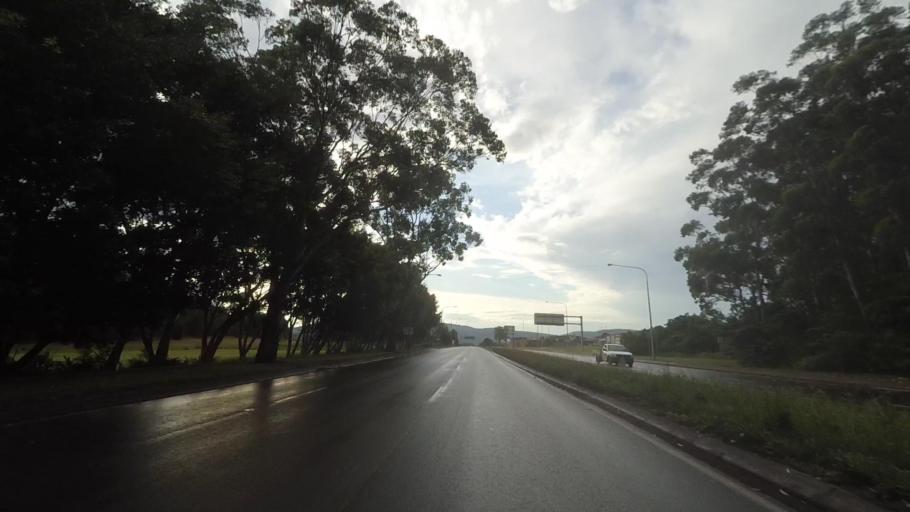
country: AU
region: New South Wales
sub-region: Wollongong
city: Mount Saint Thomas
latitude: -34.4455
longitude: 150.8743
